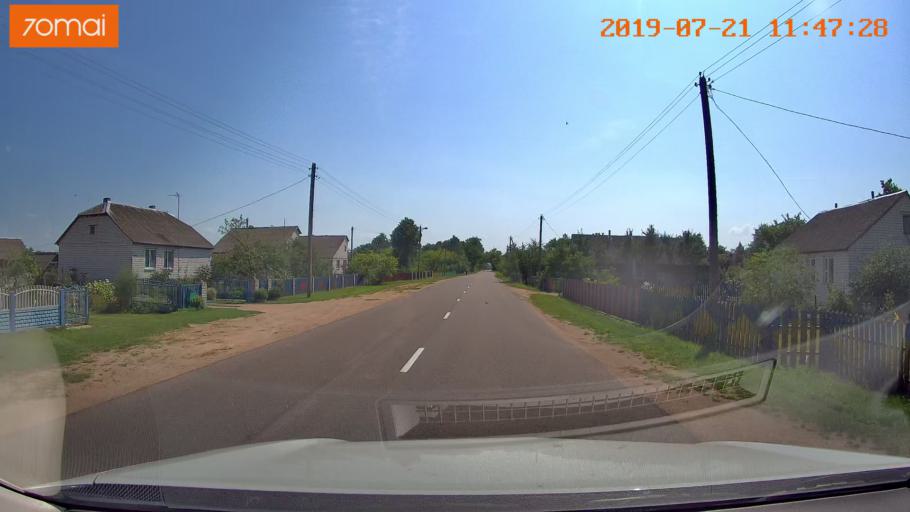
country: BY
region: Grodnenskaya
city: Lyubcha
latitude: 53.9026
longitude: 26.0478
